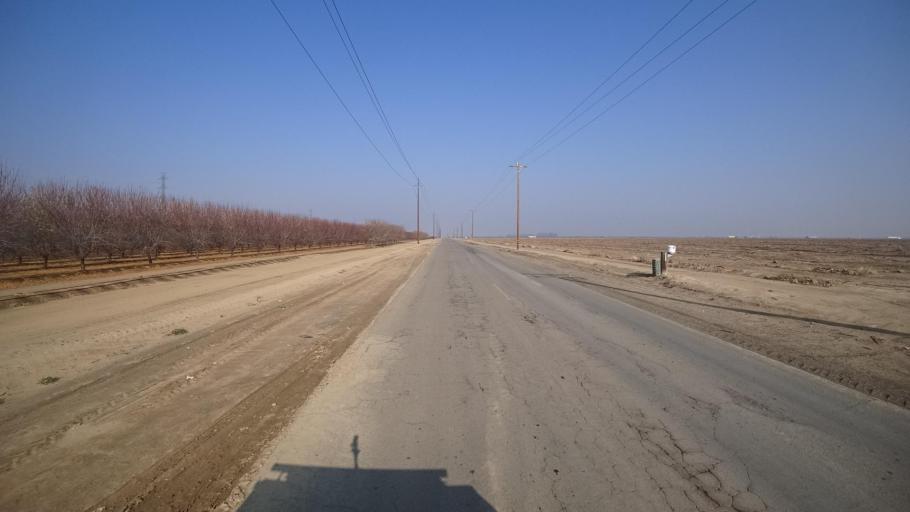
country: US
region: California
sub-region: Kern County
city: Buttonwillow
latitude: 35.4245
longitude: -119.4472
